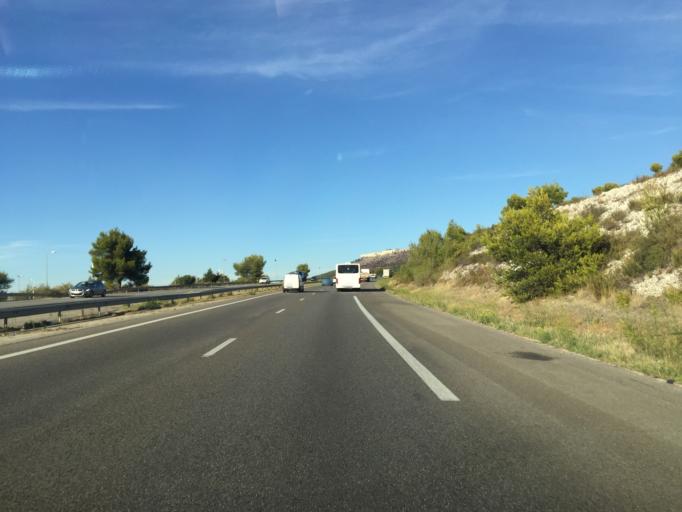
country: FR
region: Provence-Alpes-Cote d'Azur
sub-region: Departement des Bouches-du-Rhone
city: Rognac
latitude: 43.4718
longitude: 5.2345
